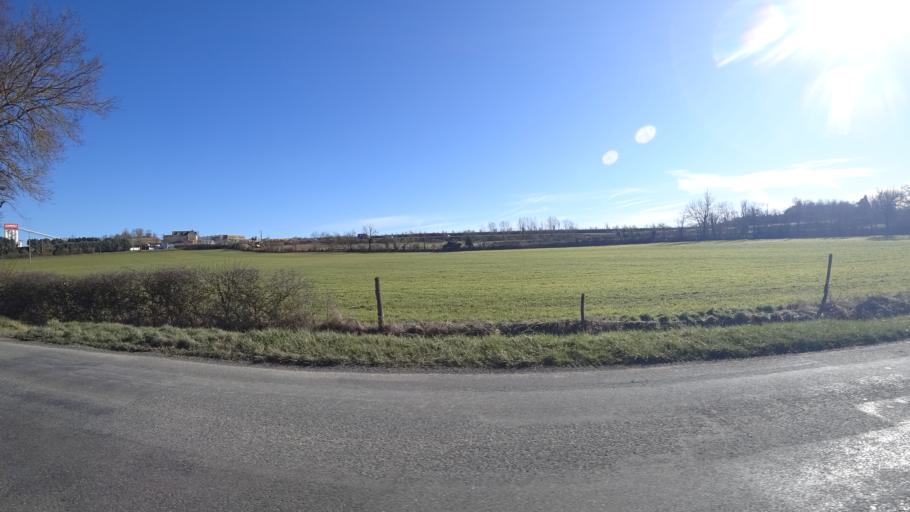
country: FR
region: Midi-Pyrenees
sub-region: Departement de l'Aveyron
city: Sebazac-Concoures
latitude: 44.3850
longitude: 2.5920
